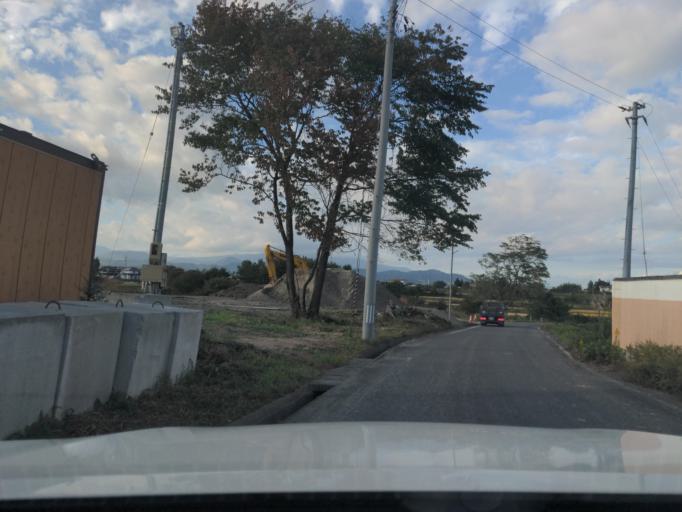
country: JP
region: Fukushima
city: Koriyama
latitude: 37.4353
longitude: 140.3647
